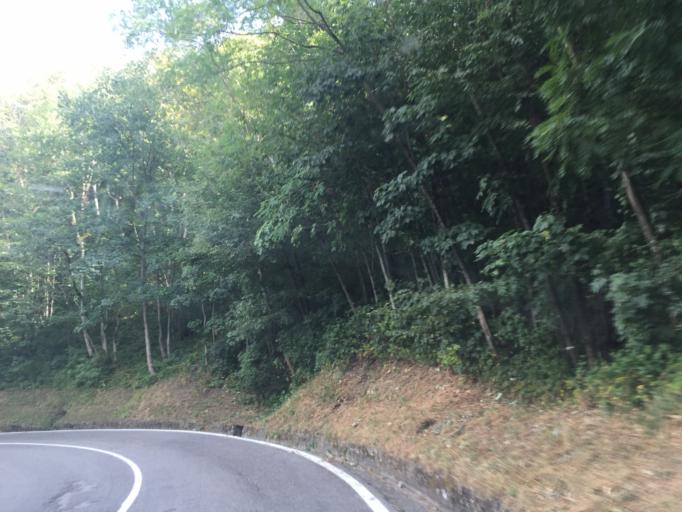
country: IT
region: Tuscany
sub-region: Provincia di Pistoia
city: Cutigliano
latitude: 44.1073
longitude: 10.7391
